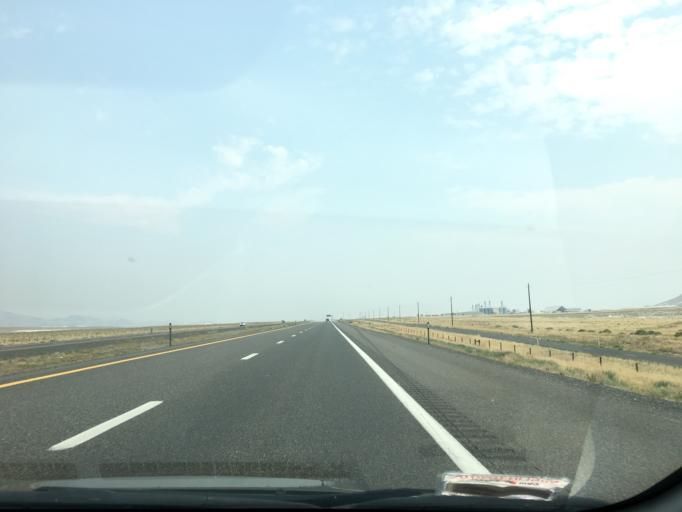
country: US
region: Nevada
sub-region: Lyon County
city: Fernley
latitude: 39.8239
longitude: -118.9839
